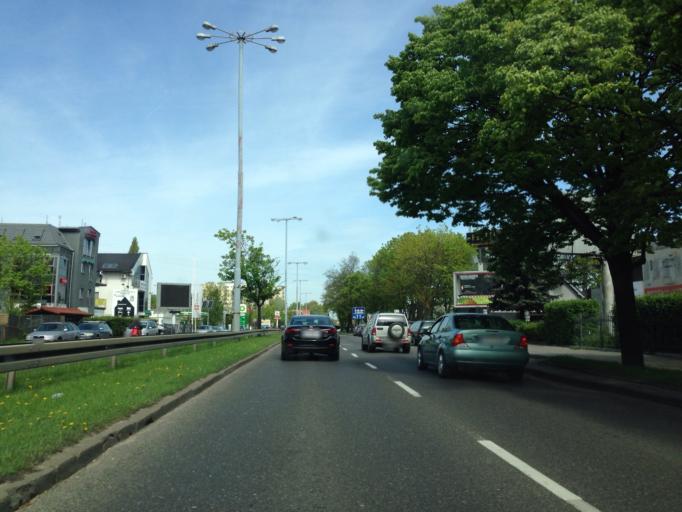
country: PL
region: Pomeranian Voivodeship
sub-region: Sopot
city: Sopot
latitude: 54.4279
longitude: 18.5626
